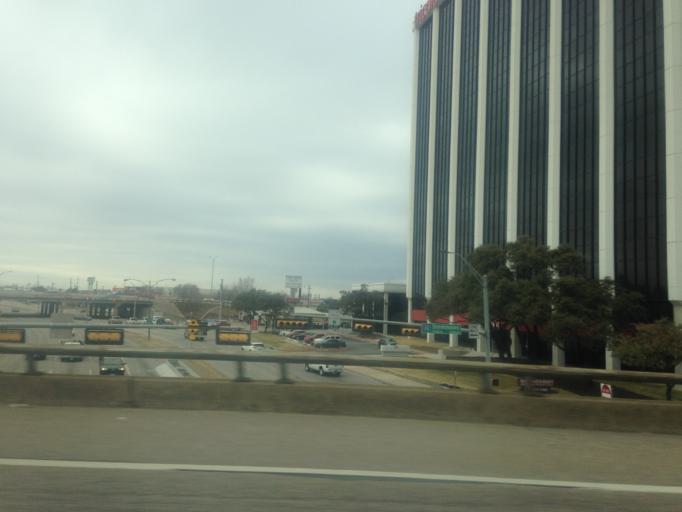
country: US
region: Texas
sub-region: Dallas County
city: Dallas
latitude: 32.8194
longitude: -96.8696
